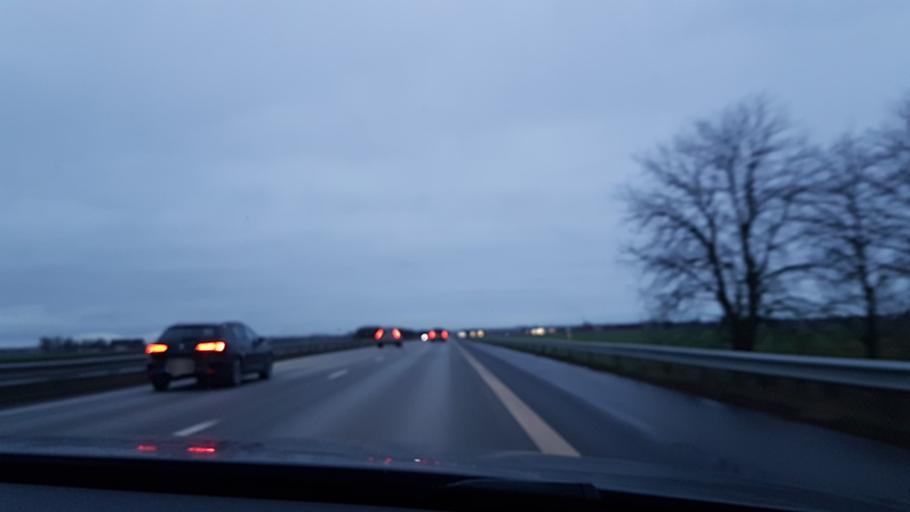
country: SE
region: Skane
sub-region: Lomma Kommun
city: Lomma
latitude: 55.7127
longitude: 13.0942
